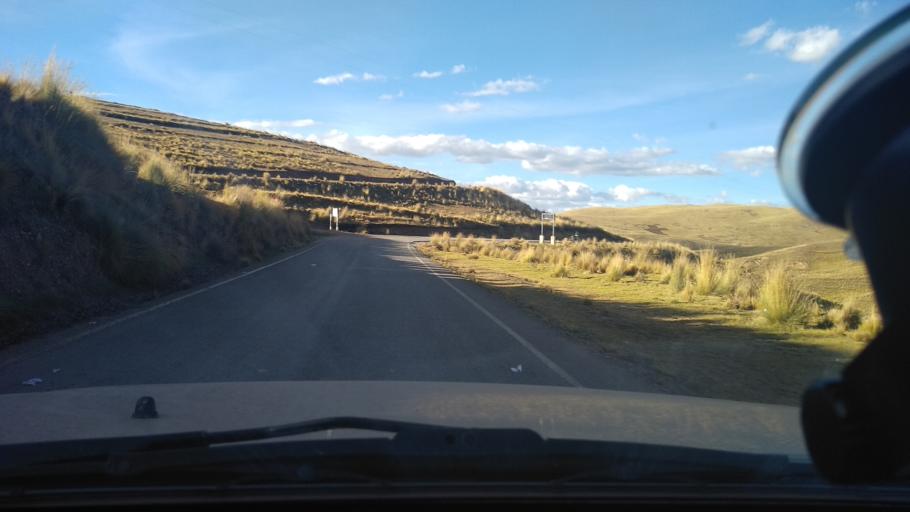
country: PE
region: Cusco
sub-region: Provincia de Canas
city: Ccaquiracunca
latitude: -14.2834
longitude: -71.4508
